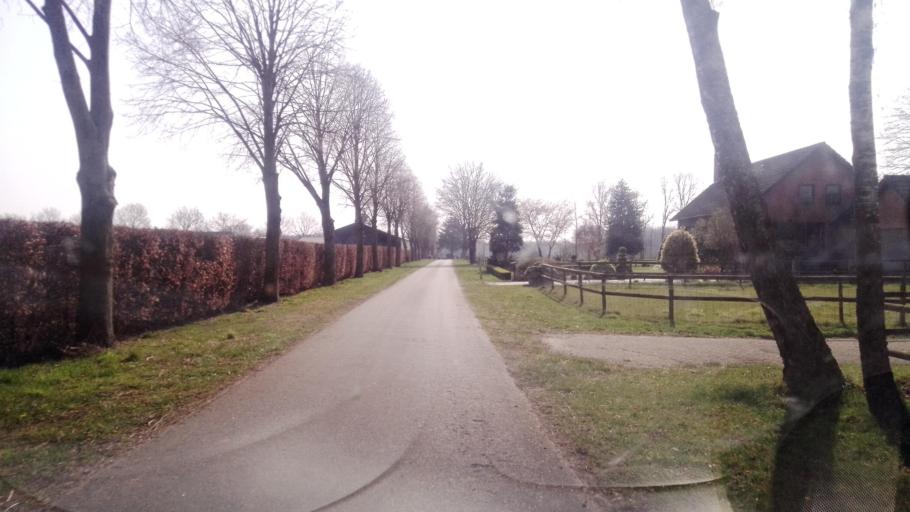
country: NL
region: Limburg
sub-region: Gemeente Peel en Maas
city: Maasbree
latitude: 51.3829
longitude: 5.9868
